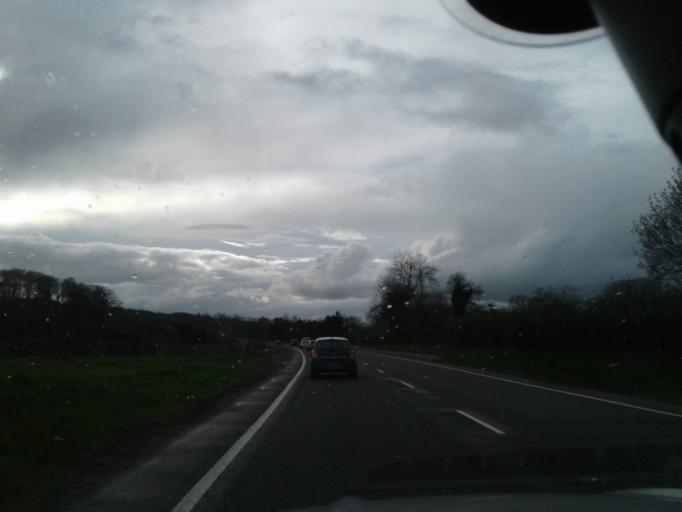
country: GB
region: Northern Ireland
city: Newtownstewart
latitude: 54.7233
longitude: -7.3824
